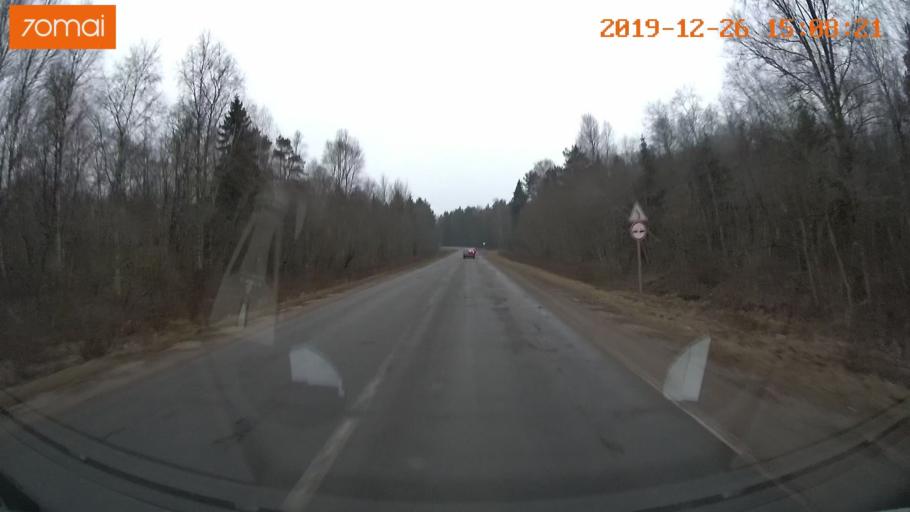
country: RU
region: Jaroslavl
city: Rybinsk
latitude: 58.1607
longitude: 38.8386
